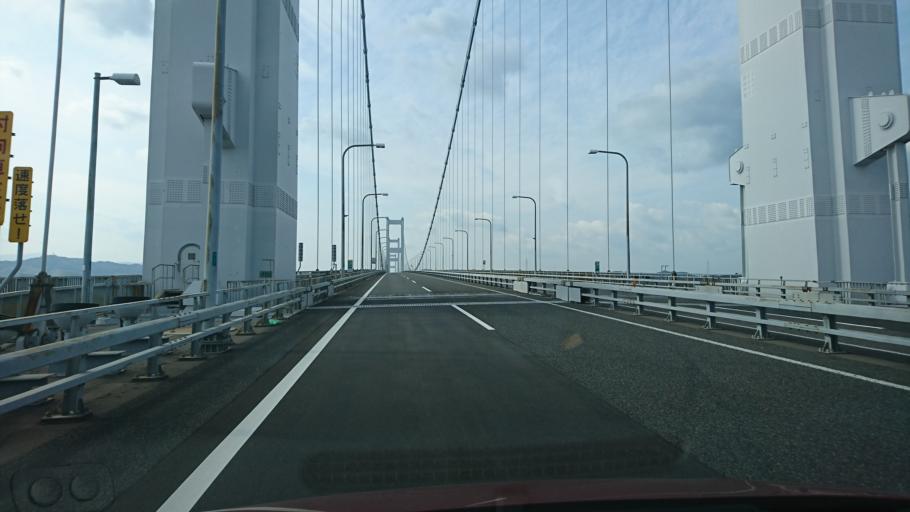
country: JP
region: Hiroshima
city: Takehara
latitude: 34.1231
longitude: 133.0053
